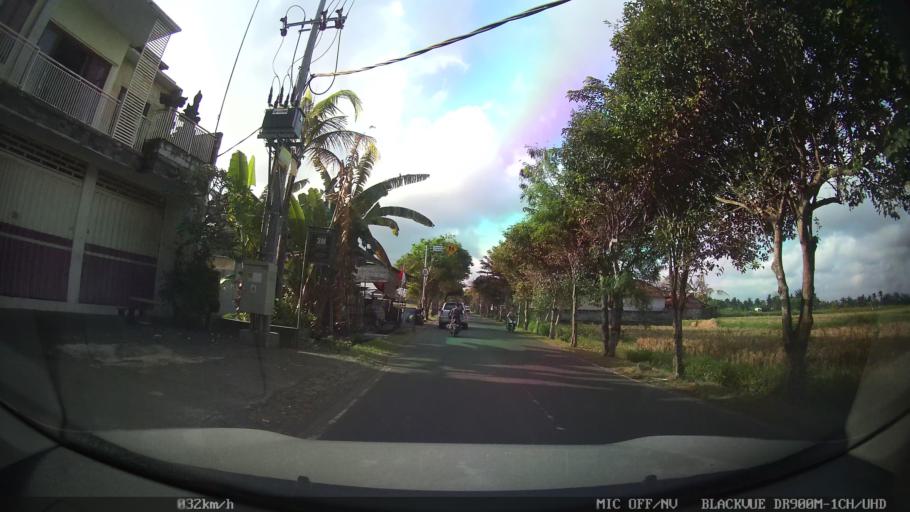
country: ID
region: Bali
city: Banjar Sedang
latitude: -8.5661
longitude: 115.2345
